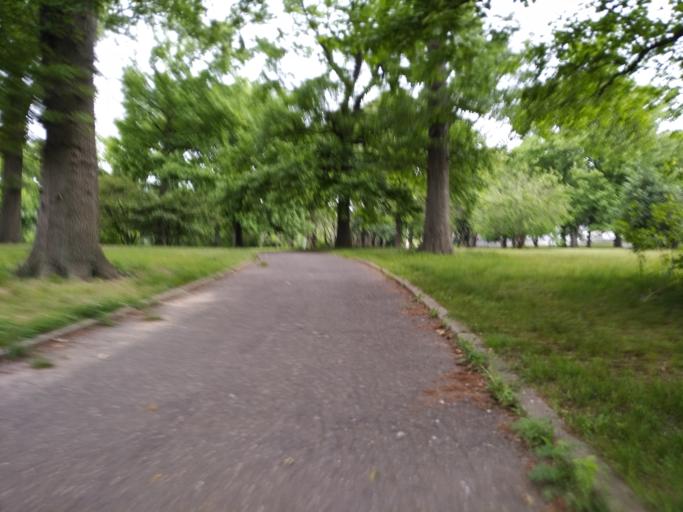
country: US
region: New York
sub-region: Queens County
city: Jamaica
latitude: 40.7467
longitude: -73.8042
